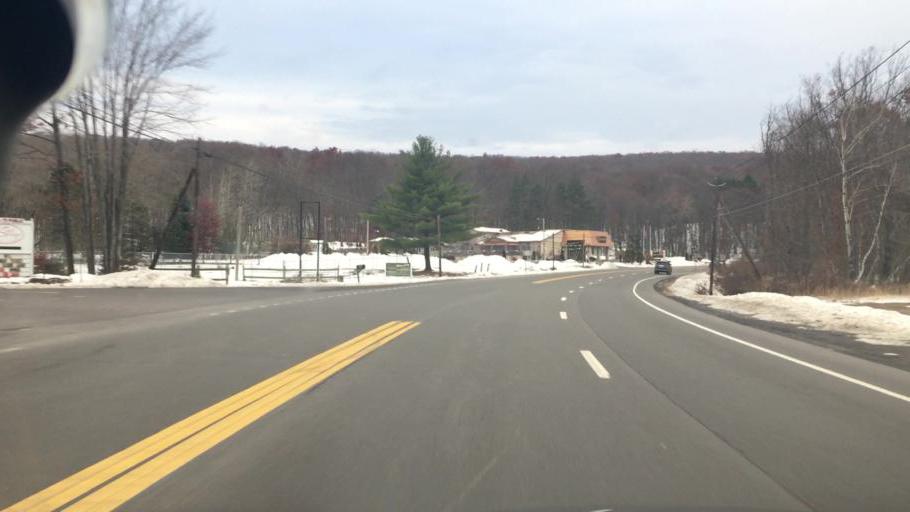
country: US
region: Pennsylvania
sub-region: Luzerne County
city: Freeland
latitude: 41.0622
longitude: -75.9636
